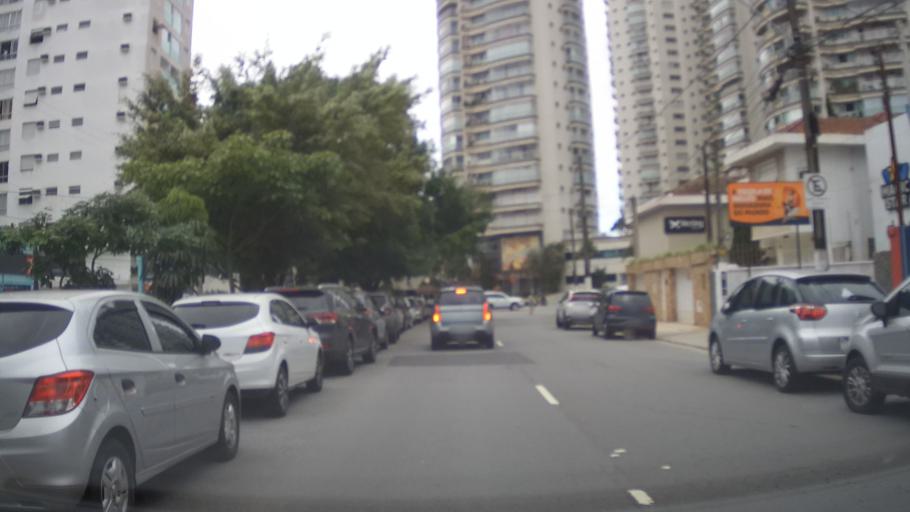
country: BR
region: Sao Paulo
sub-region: Santos
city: Santos
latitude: -23.9886
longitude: -46.3011
